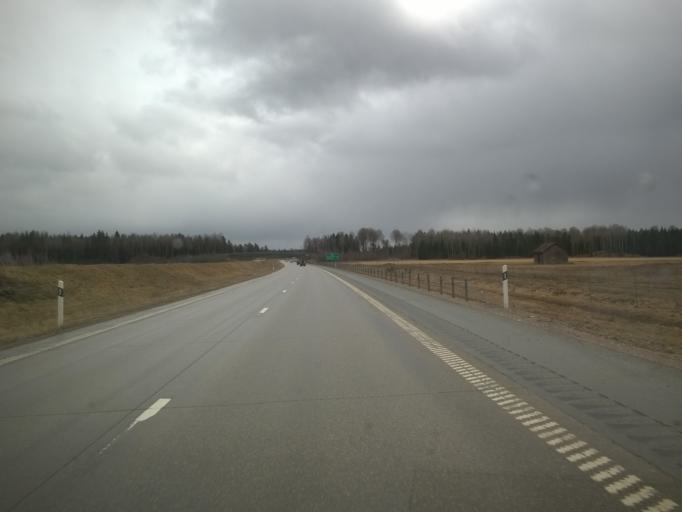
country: SE
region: Uppsala
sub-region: Osthammars Kommun
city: Bjorklinge
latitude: 60.0046
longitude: 17.6283
